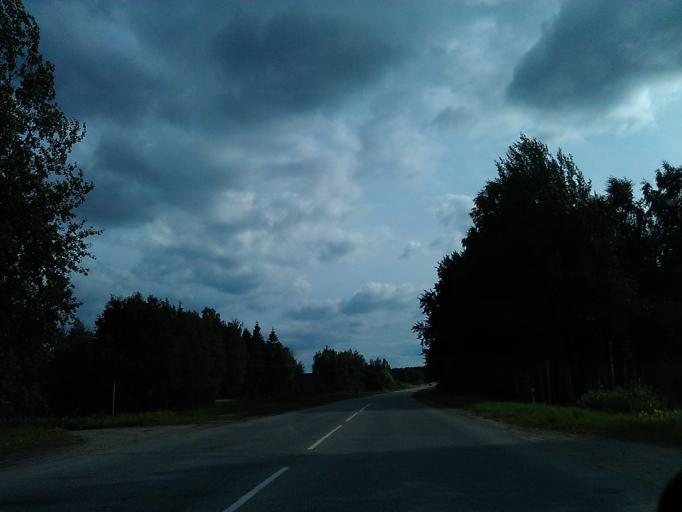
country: LV
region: Cesu Rajons
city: Cesis
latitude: 57.2921
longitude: 25.3033
